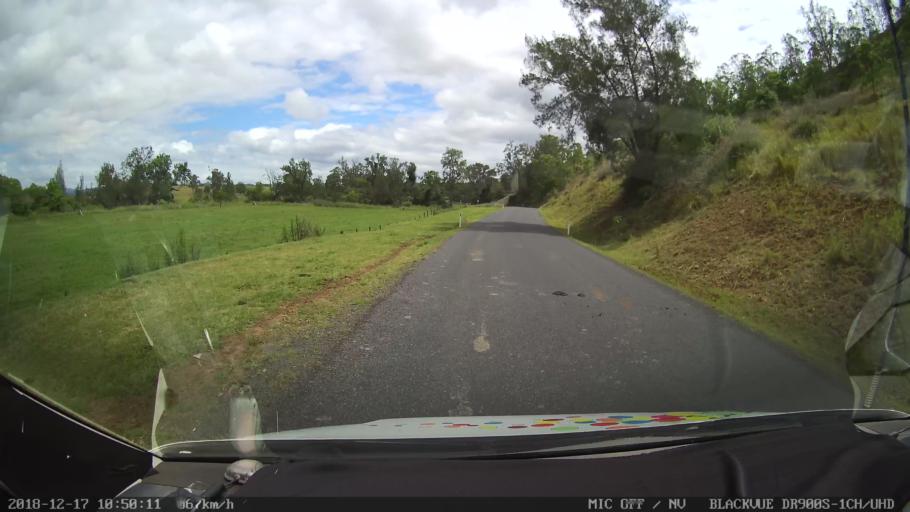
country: AU
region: New South Wales
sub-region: Clarence Valley
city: Gordon
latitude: -28.8613
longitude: 152.5742
